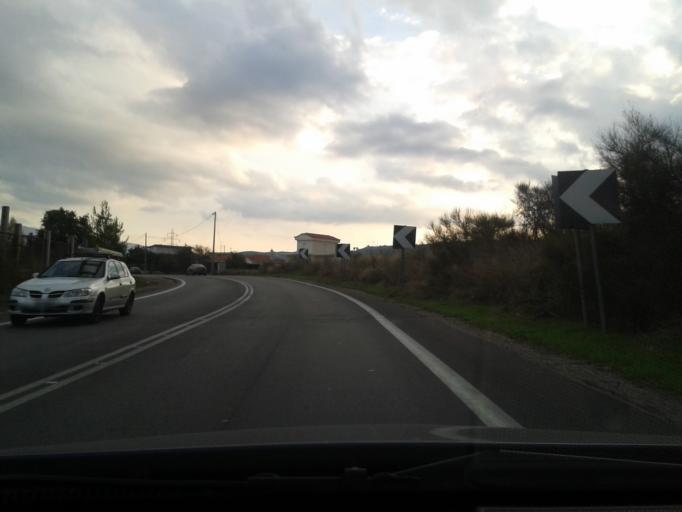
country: GR
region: Attica
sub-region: Nomarchia Anatolikis Attikis
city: Afidnes
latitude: 38.1965
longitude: 23.8527
